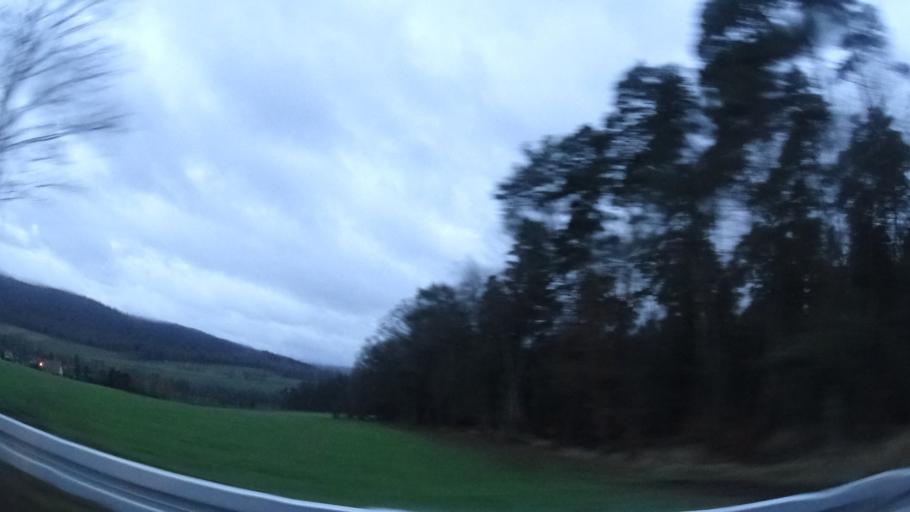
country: DE
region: Hesse
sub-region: Regierungsbezirk Kassel
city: Eichenzell
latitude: 50.4764
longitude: 9.6946
